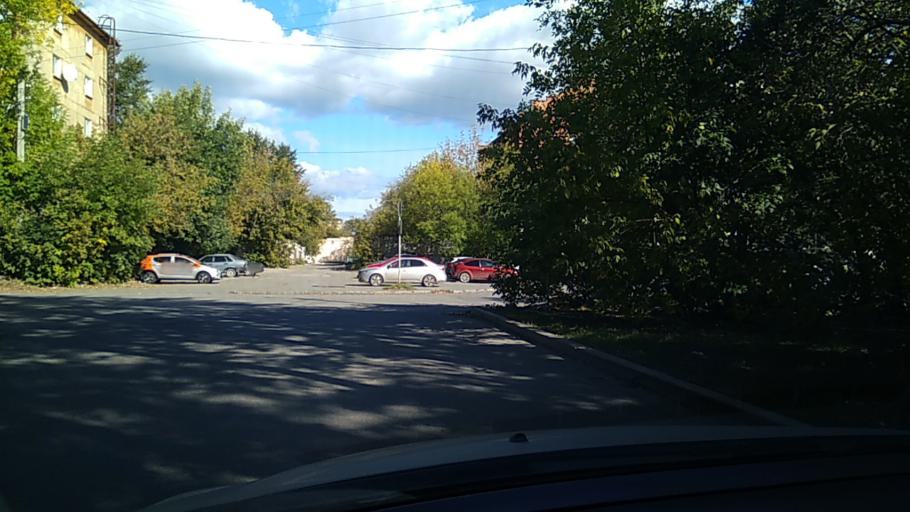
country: RU
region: Sverdlovsk
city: Yekaterinburg
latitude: 56.8836
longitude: 60.5765
